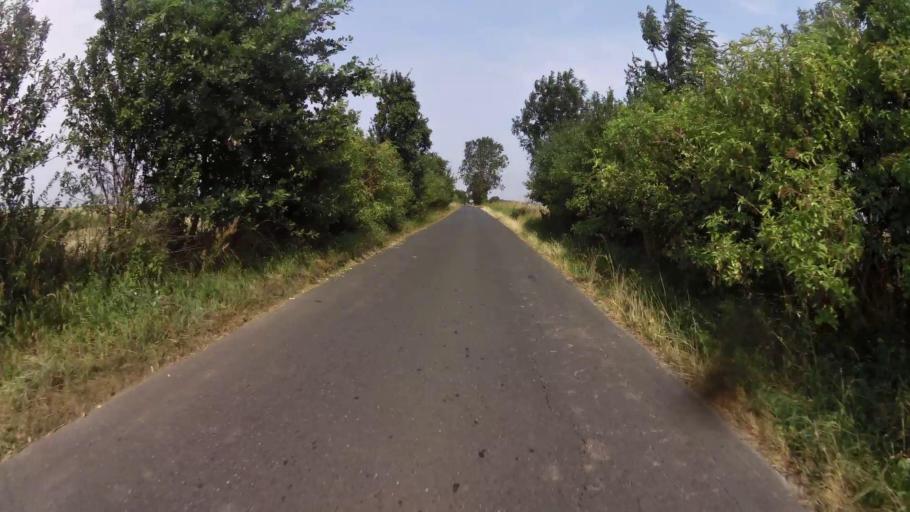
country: PL
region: West Pomeranian Voivodeship
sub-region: Powiat pyrzycki
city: Lipiany
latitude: 52.9808
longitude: 15.0332
